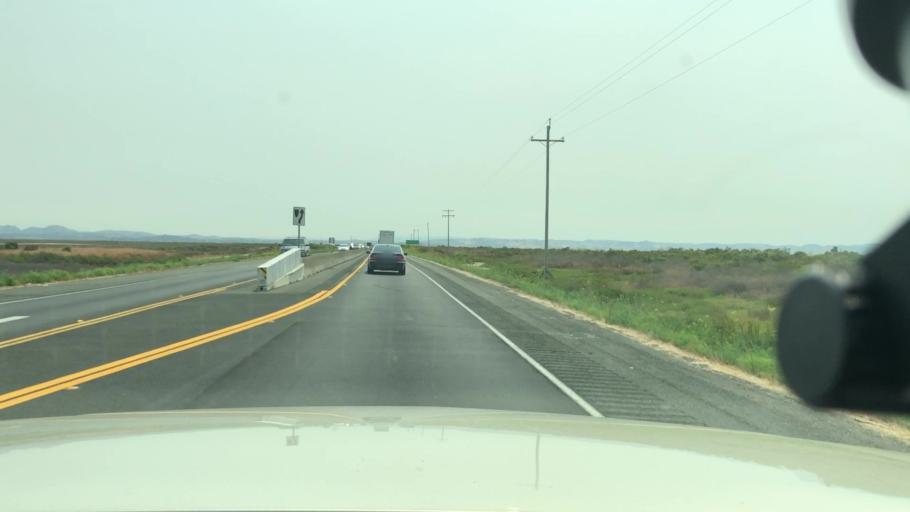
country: US
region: California
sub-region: Napa County
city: American Canyon
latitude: 38.1484
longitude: -122.3803
